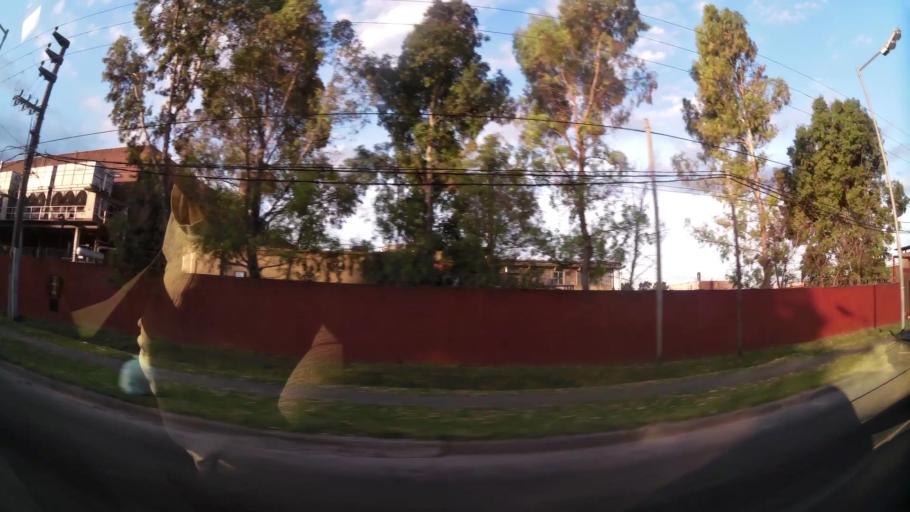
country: AR
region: Buenos Aires
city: Santa Catalina - Dique Lujan
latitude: -34.4502
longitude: -58.6609
